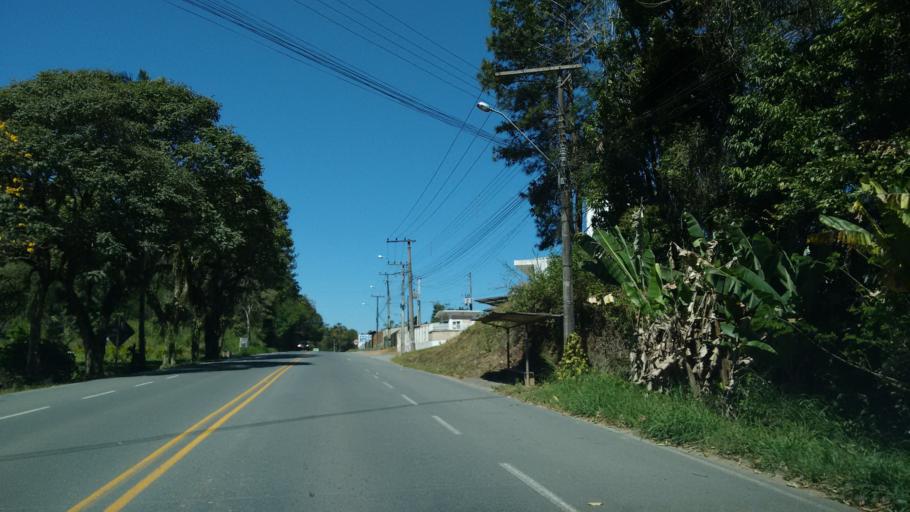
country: BR
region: Santa Catarina
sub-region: Indaial
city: Indaial
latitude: -26.8562
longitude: -49.1536
